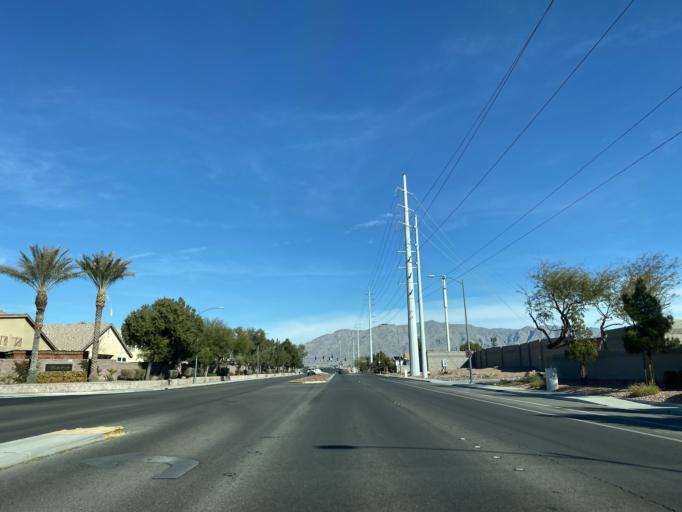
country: US
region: Nevada
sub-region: Clark County
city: North Las Vegas
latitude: 36.2700
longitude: -115.2252
